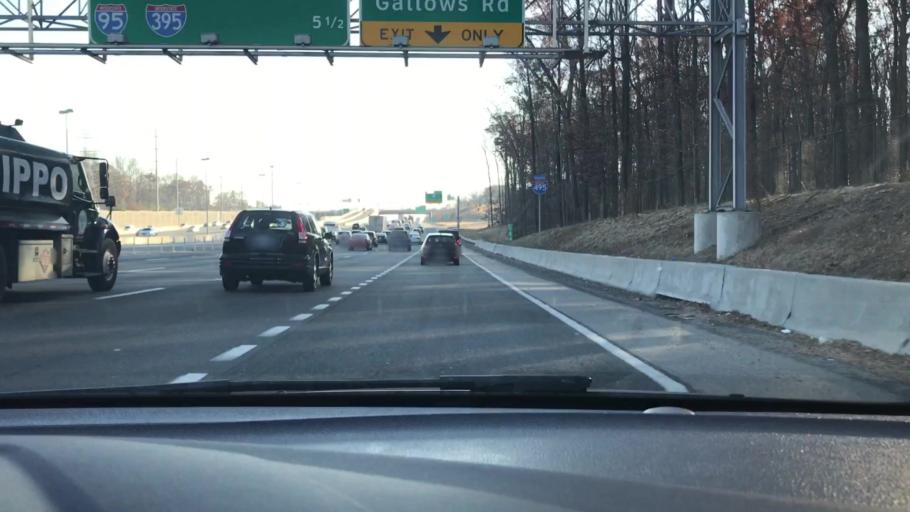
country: US
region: Virginia
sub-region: Fairfax County
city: Merrifield
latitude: 38.8592
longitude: -77.2205
